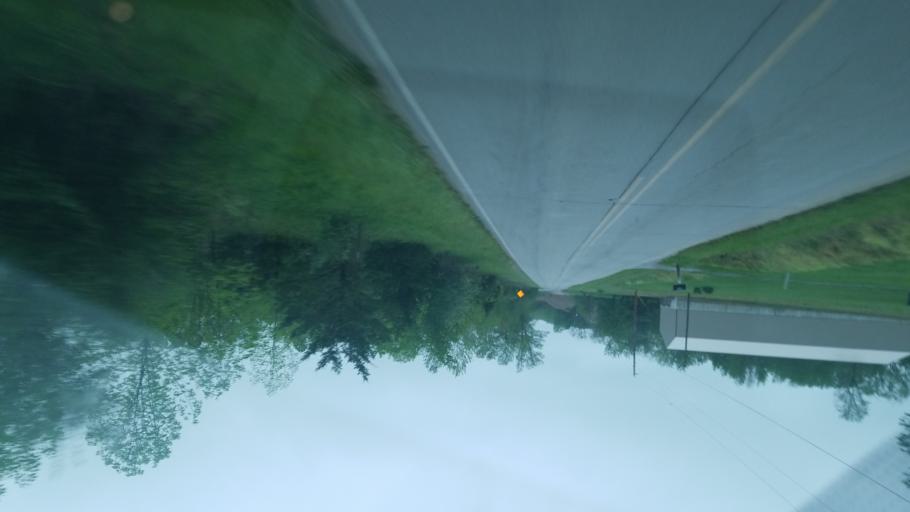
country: US
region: Ohio
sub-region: Highland County
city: Hillsboro
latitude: 39.1742
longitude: -83.6363
